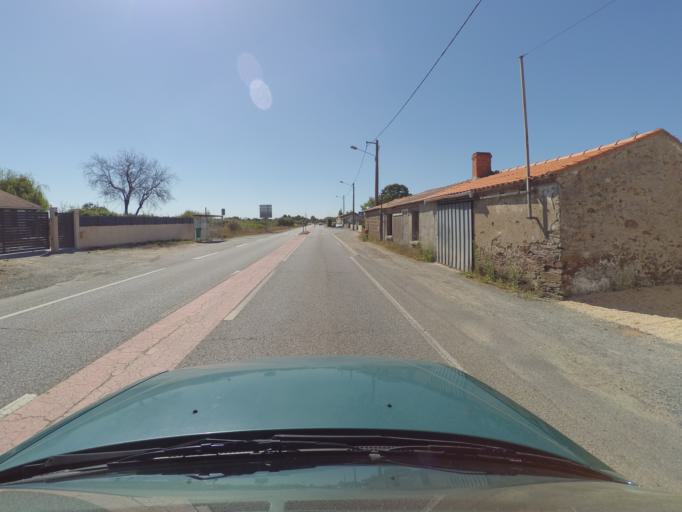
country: FR
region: Pays de la Loire
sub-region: Departement de la Loire-Atlantique
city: Les Sorinieres
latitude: 47.1154
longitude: -1.5413
